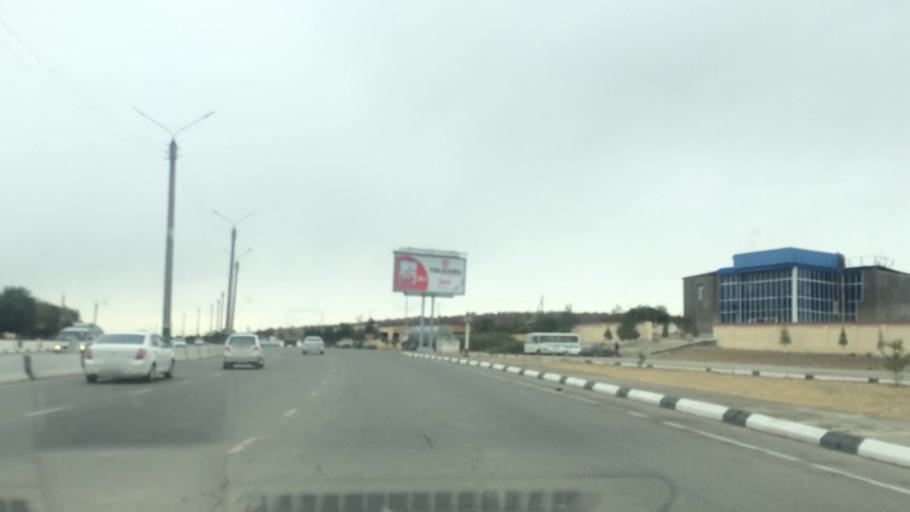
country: UZ
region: Samarqand
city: Jomboy
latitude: 39.6757
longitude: 67.0419
